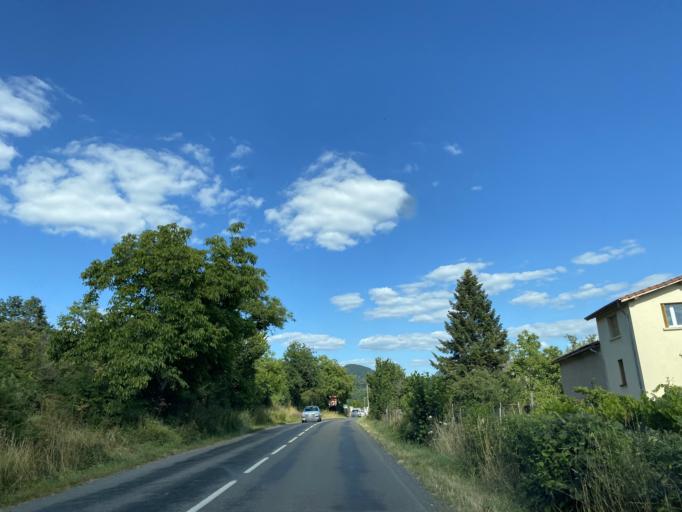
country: FR
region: Auvergne
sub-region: Departement du Puy-de-Dome
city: Peschadoires
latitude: 45.8649
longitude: 3.5010
